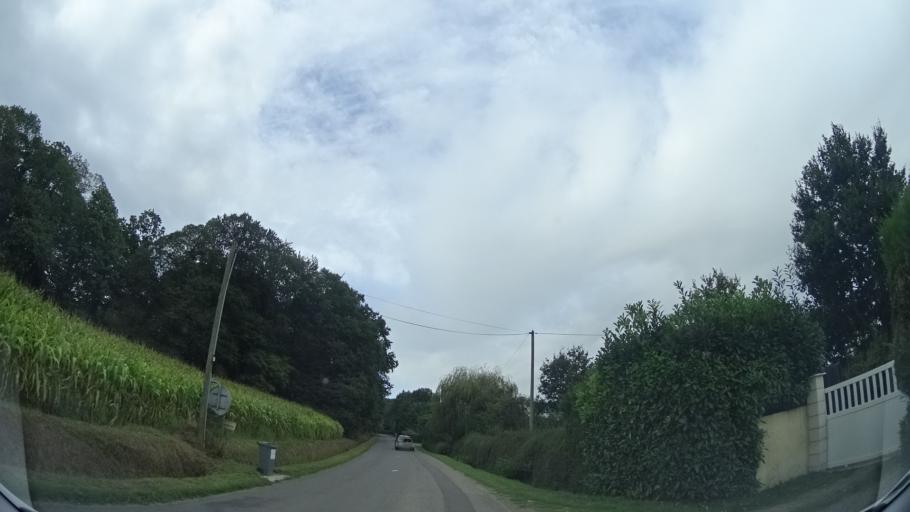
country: FR
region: Brittany
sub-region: Departement d'Ille-et-Vilaine
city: Hede-Bazouges
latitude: 48.3010
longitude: -1.7921
